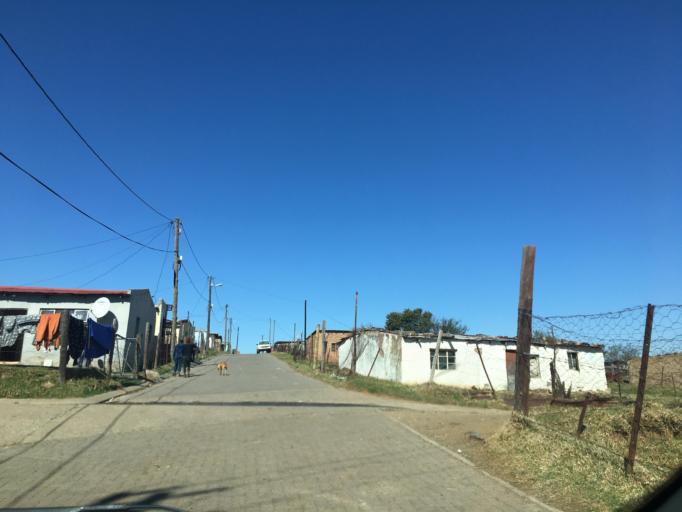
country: ZA
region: Eastern Cape
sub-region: Chris Hani District Municipality
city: Elliot
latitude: -31.3375
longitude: 27.8604
